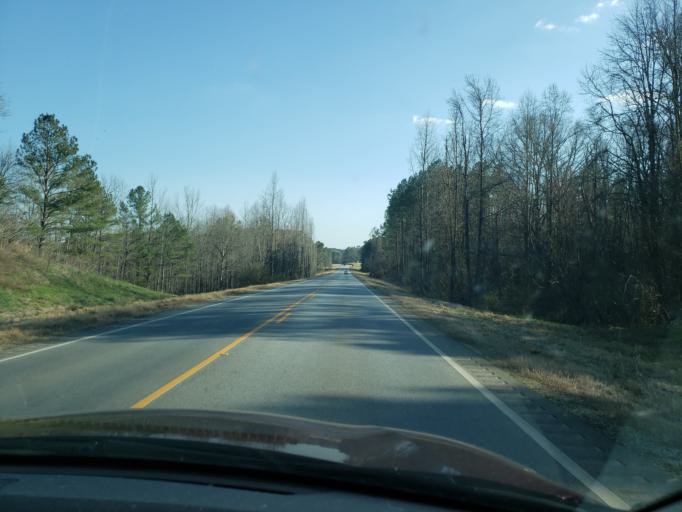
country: US
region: Alabama
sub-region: Randolph County
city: Wedowee
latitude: 33.4210
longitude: -85.5499
